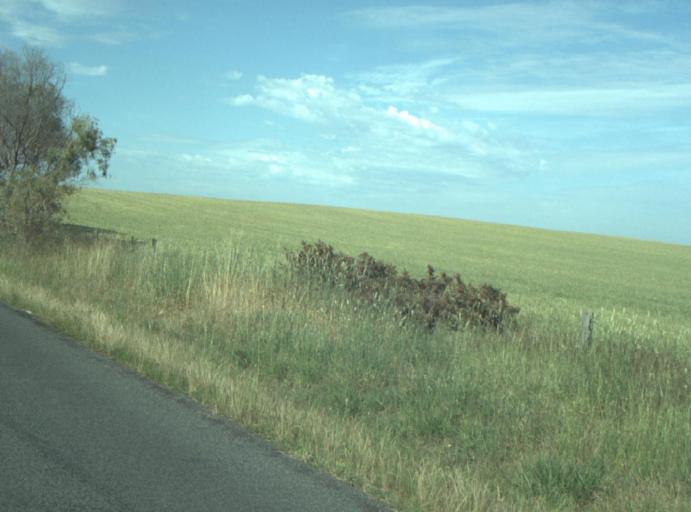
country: AU
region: Victoria
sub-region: Greater Geelong
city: Clifton Springs
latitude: -38.1749
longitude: 144.5141
